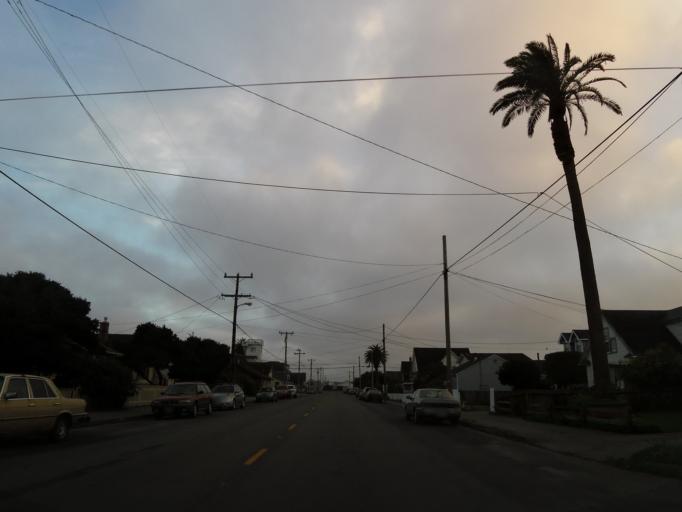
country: US
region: California
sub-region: Mendocino County
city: Fort Bragg
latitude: 39.4491
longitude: -123.8073
